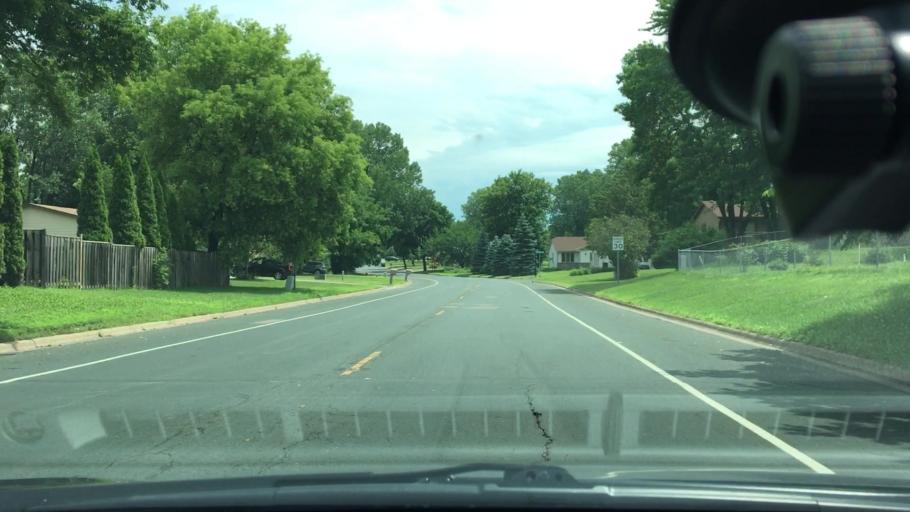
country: US
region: Minnesota
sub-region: Hennepin County
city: Maple Grove
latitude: 45.0670
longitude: -93.4355
